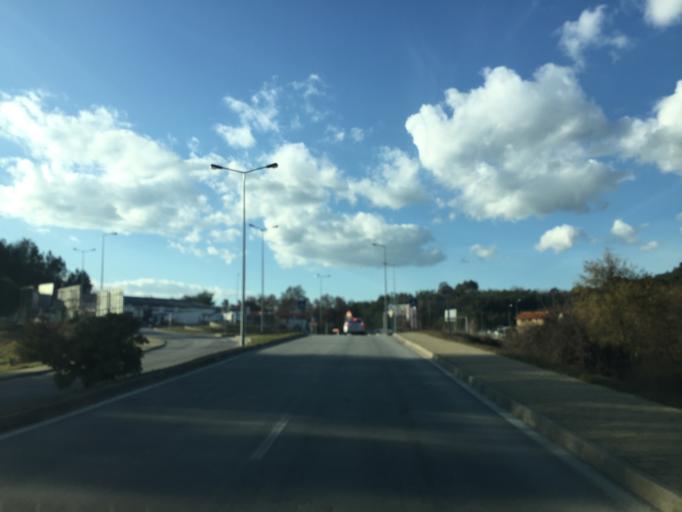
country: PT
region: Guarda
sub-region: Seia
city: Seia
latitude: 40.4307
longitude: -7.7171
